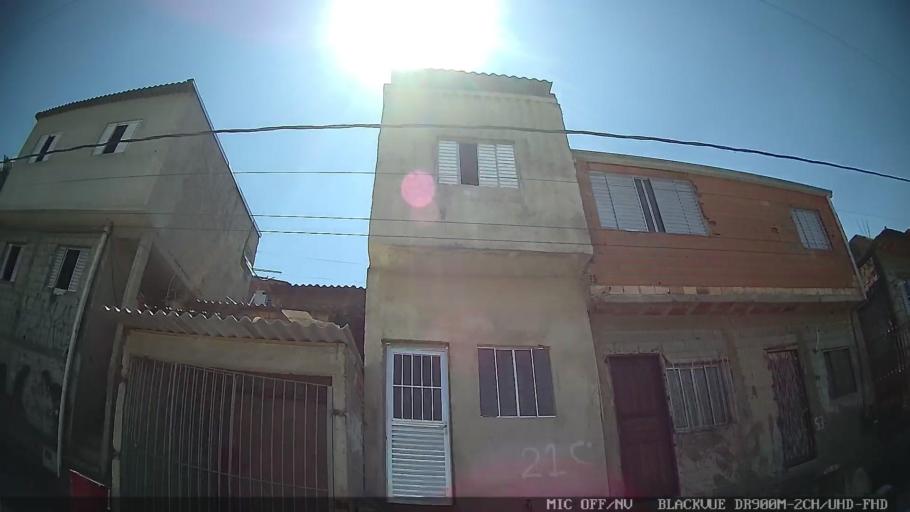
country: BR
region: Sao Paulo
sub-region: Sao Caetano Do Sul
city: Sao Caetano do Sul
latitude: -23.5684
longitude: -46.5184
